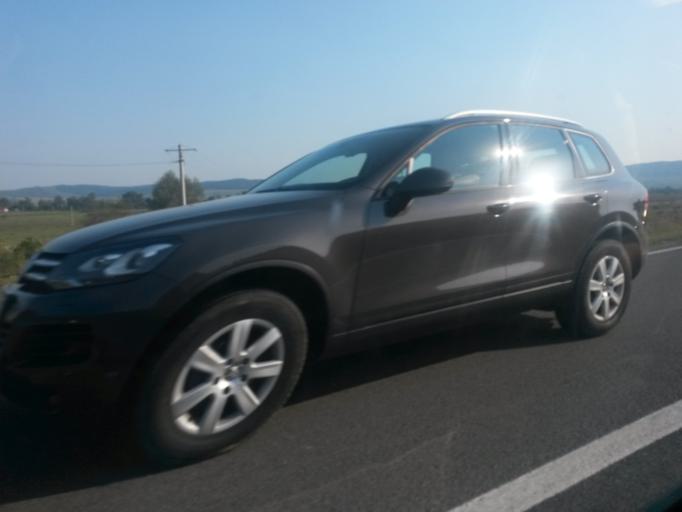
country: RO
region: Alba
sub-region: Comuna Unirea
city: Unirea
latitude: 46.3959
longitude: 23.7952
